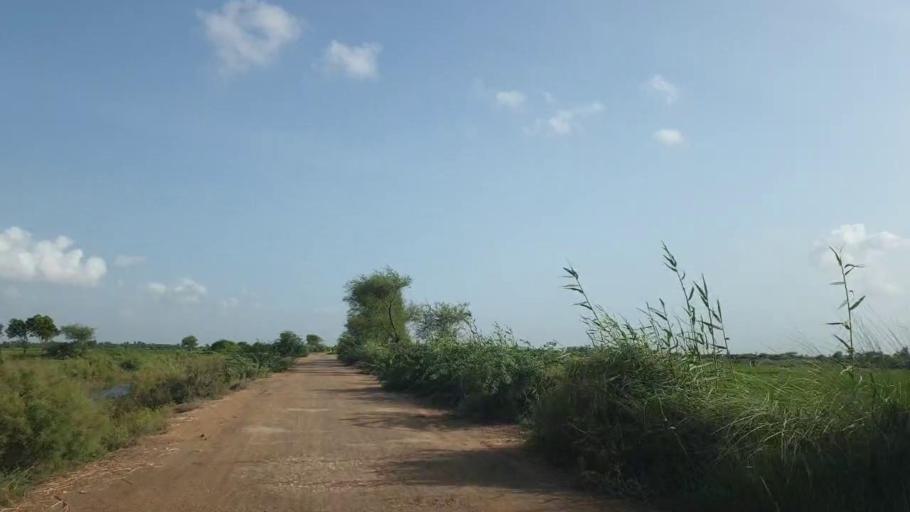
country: PK
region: Sindh
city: Kadhan
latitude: 24.6174
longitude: 69.0959
